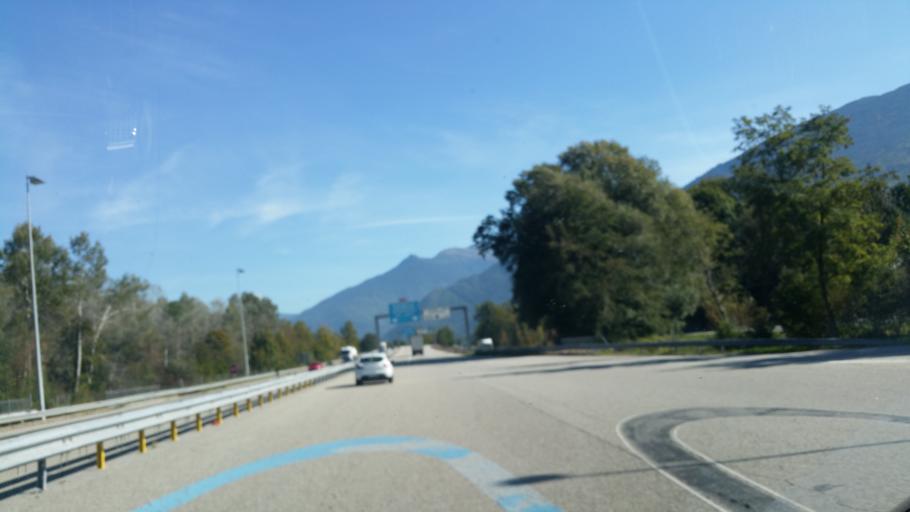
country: FR
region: Rhone-Alpes
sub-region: Departement de la Savoie
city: Sainte-Helene-sur-Isere
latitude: 45.6212
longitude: 6.3146
